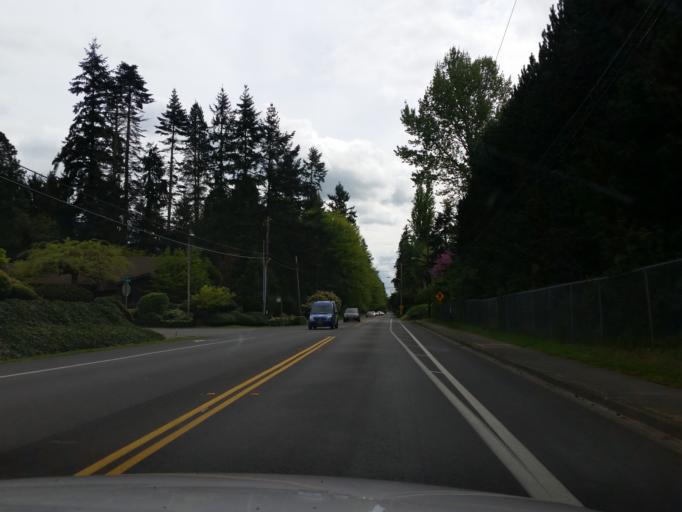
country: US
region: Washington
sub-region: King County
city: Kingsgate
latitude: 47.7036
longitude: -122.1645
